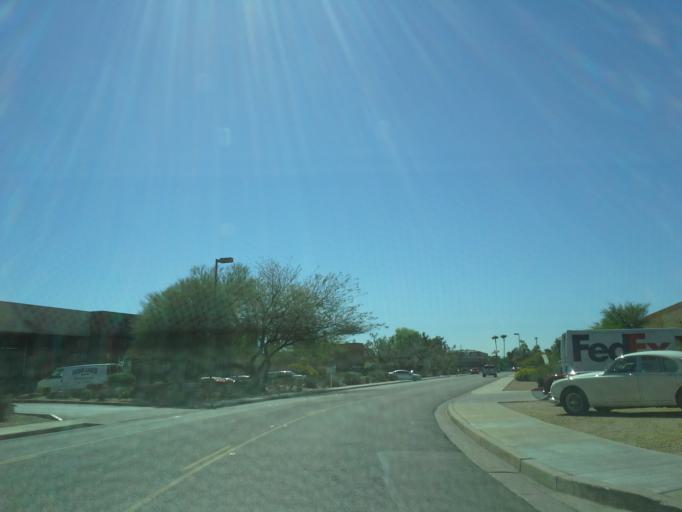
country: US
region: Arizona
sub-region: Maricopa County
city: Paradise Valley
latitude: 33.6214
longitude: -111.9013
